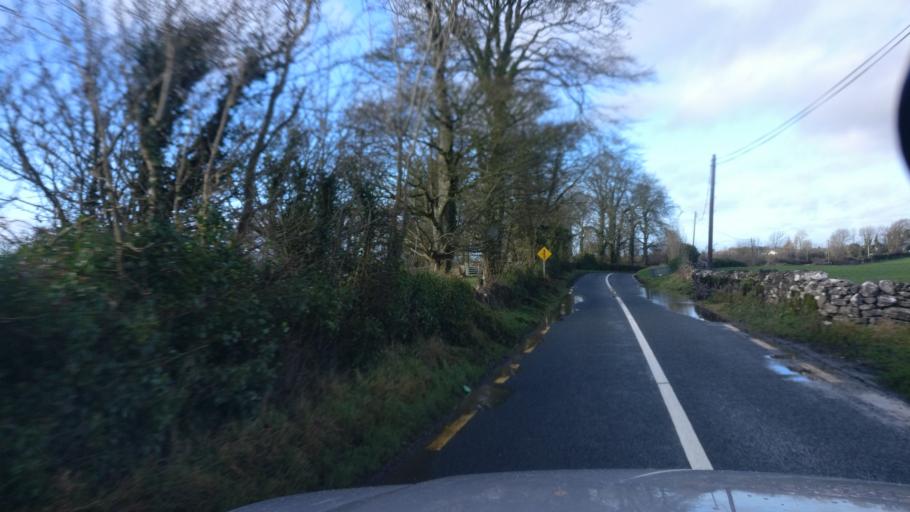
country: IE
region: Connaught
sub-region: County Galway
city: Athenry
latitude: 53.2550
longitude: -8.6778
